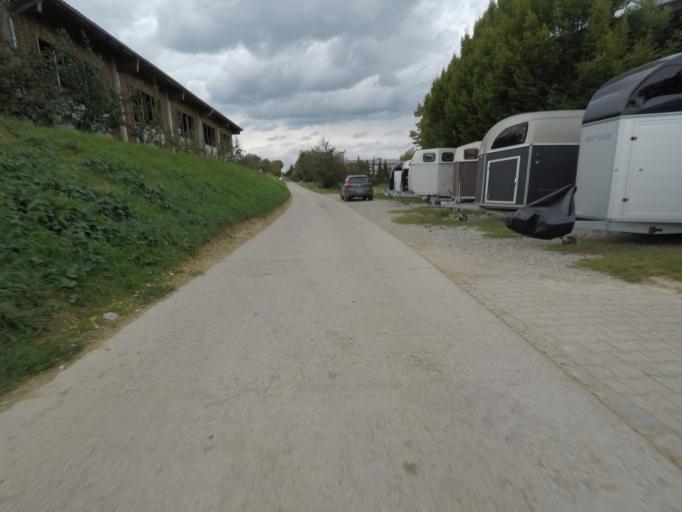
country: DE
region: Baden-Wuerttemberg
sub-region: Regierungsbezirk Stuttgart
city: Filderstadt
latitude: 48.6625
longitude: 9.1913
